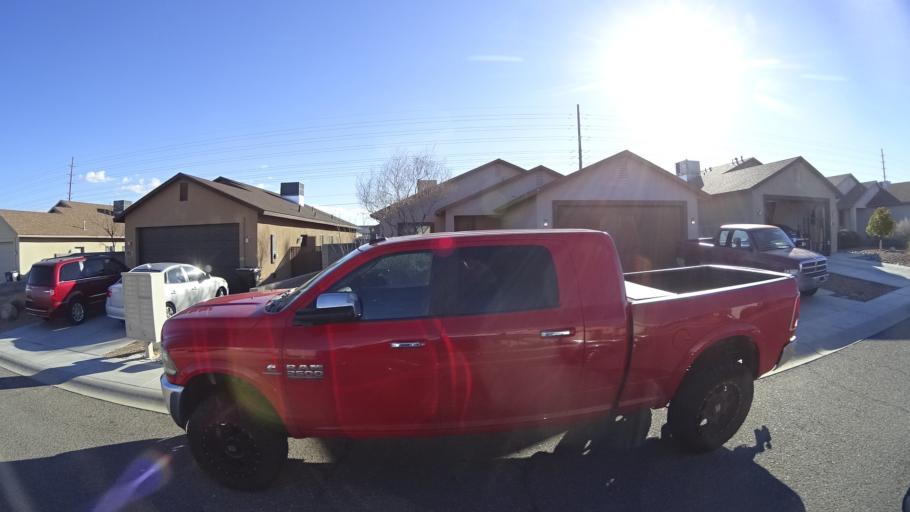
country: US
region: Arizona
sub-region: Mohave County
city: New Kingman-Butler
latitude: 35.2220
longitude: -113.9943
